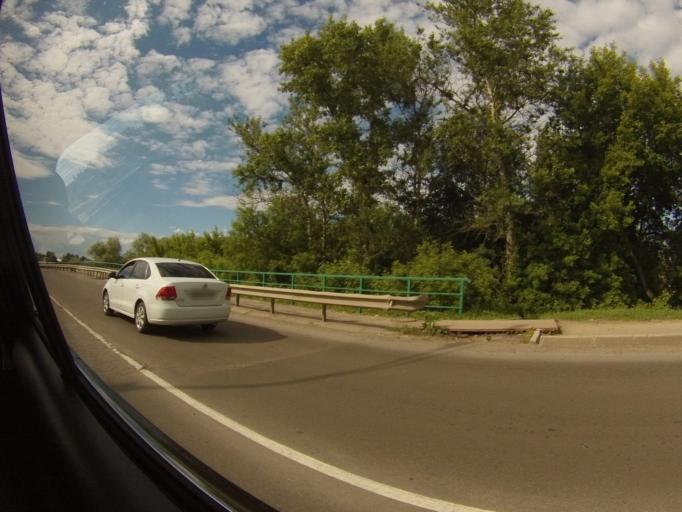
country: RU
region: Orjol
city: Mtsensk
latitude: 53.2826
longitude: 36.5669
